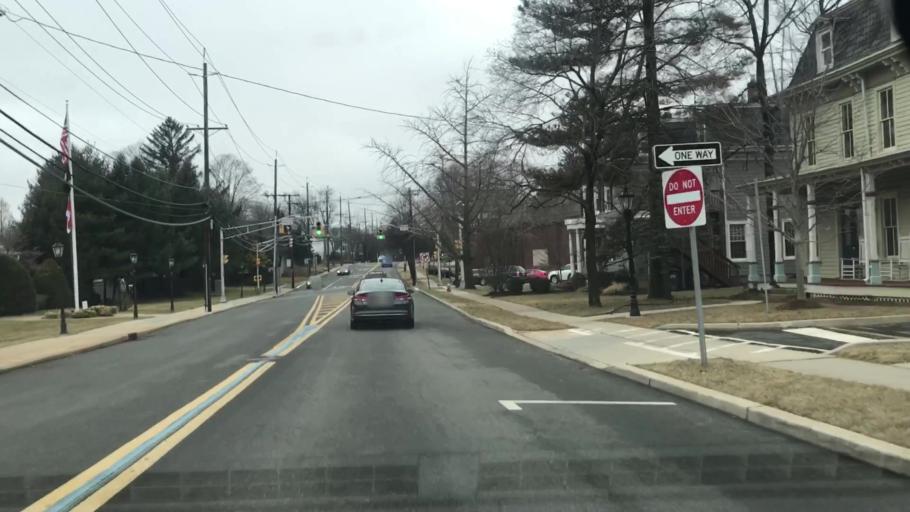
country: US
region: New Jersey
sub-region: Bergen County
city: Westwood
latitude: 40.9920
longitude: -74.0355
